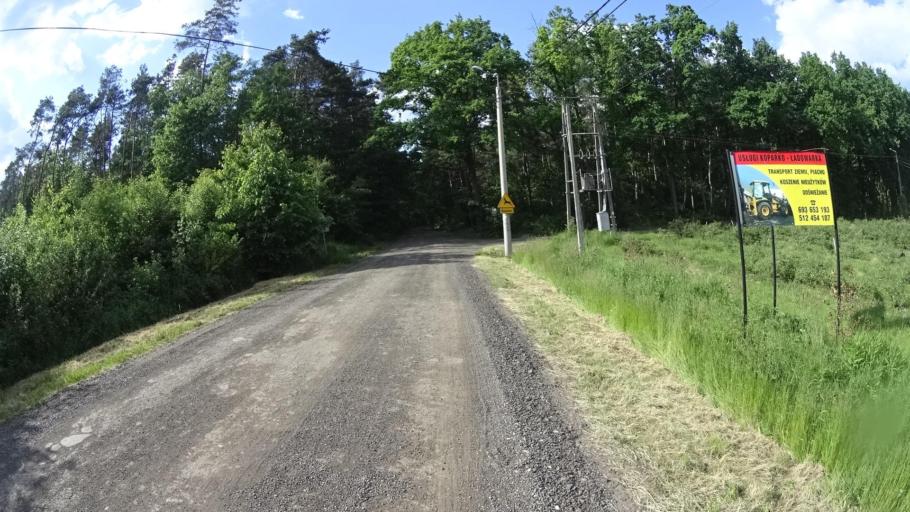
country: PL
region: Masovian Voivodeship
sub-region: Powiat pruszkowski
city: Nadarzyn
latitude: 52.0623
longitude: 20.8218
